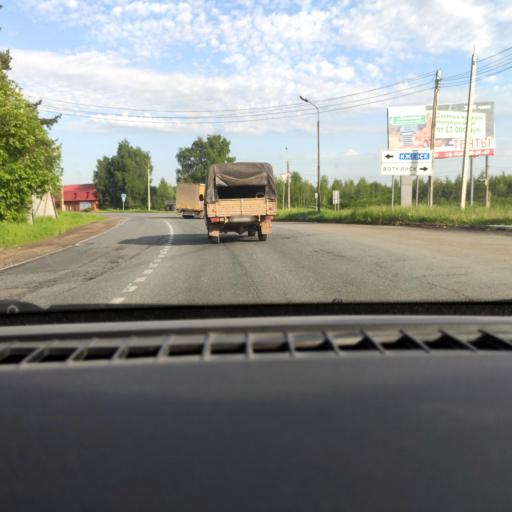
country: RU
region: Udmurtiya
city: Votkinsk
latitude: 57.0332
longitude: 53.9399
